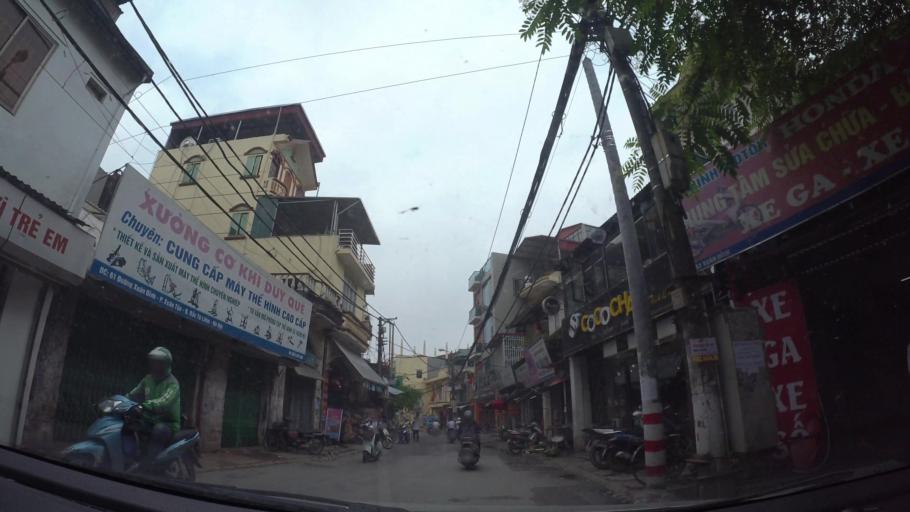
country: VN
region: Ha Noi
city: Tay Ho
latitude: 21.0703
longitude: 105.8014
